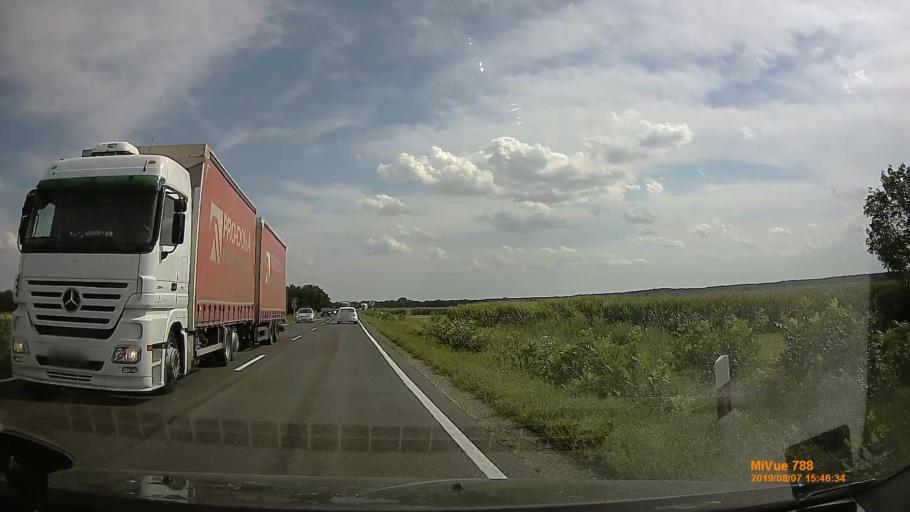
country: HU
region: Vas
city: Szombathely
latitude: 47.1837
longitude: 16.6219
